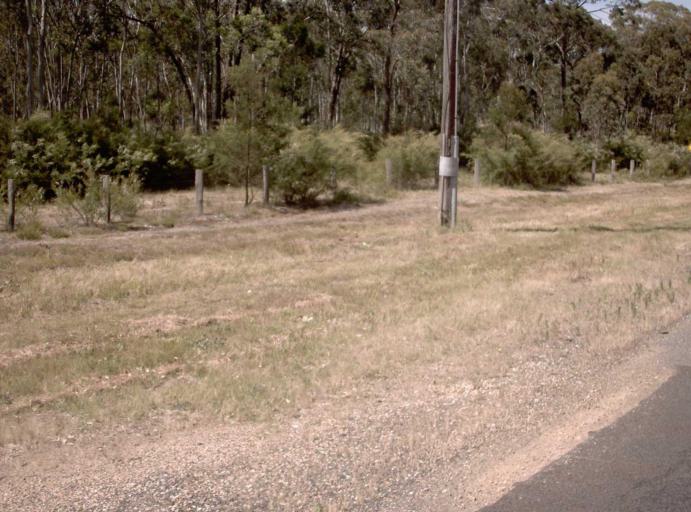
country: AU
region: Victoria
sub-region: East Gippsland
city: Bairnsdale
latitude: -37.9088
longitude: 147.3196
